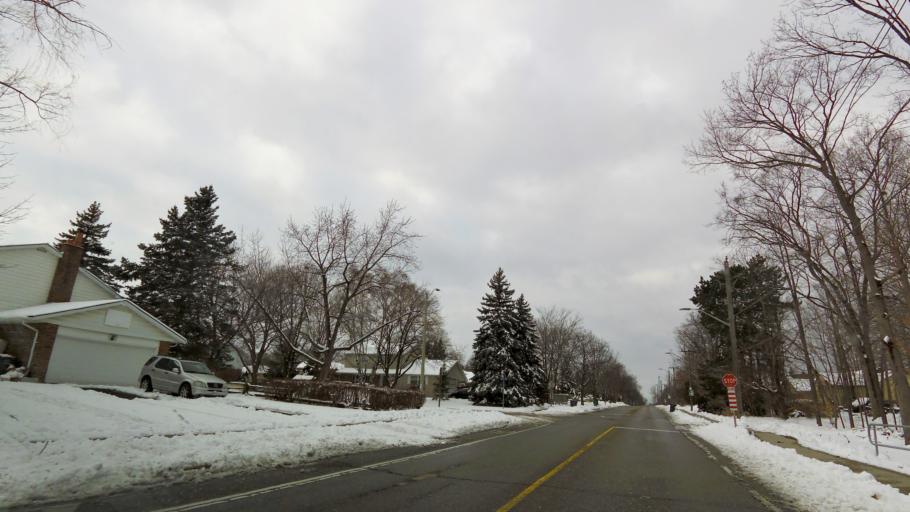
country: CA
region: Ontario
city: Mississauga
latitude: 43.5317
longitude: -79.6620
